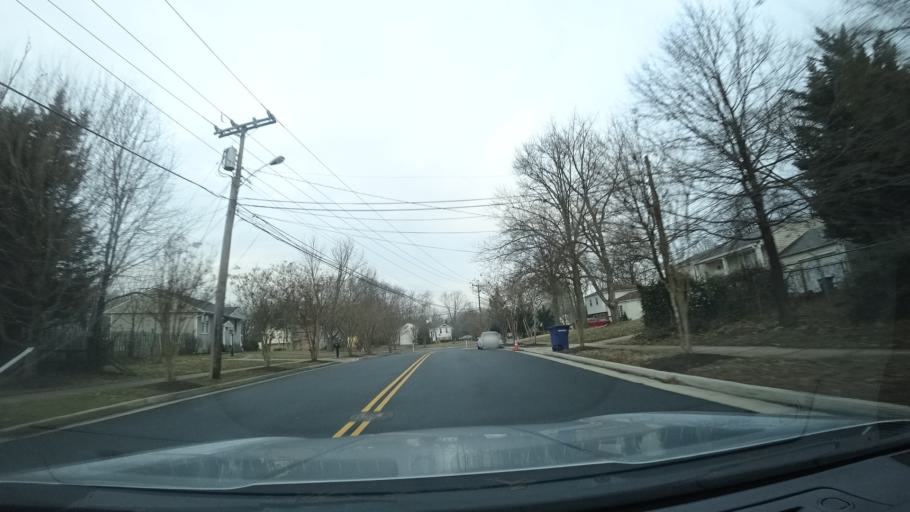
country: US
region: Virginia
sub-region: Fairfax County
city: Herndon
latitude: 38.9610
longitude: -77.3872
